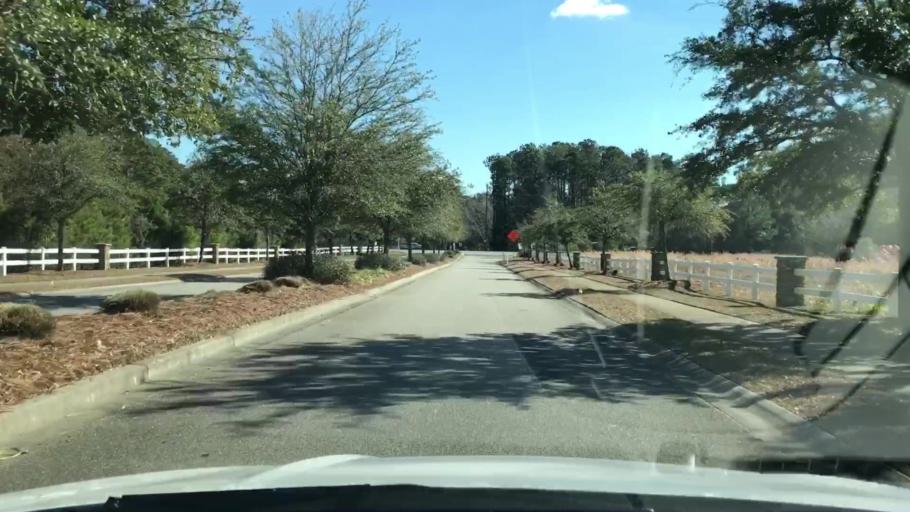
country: US
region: South Carolina
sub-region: Horry County
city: Garden City
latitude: 33.6411
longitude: -79.0321
